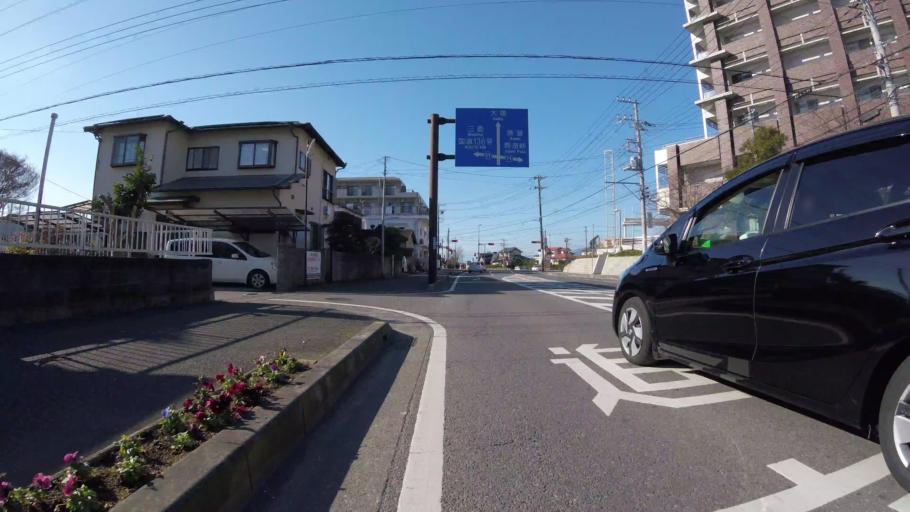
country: JP
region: Shizuoka
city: Mishima
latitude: 35.0884
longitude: 138.9535
